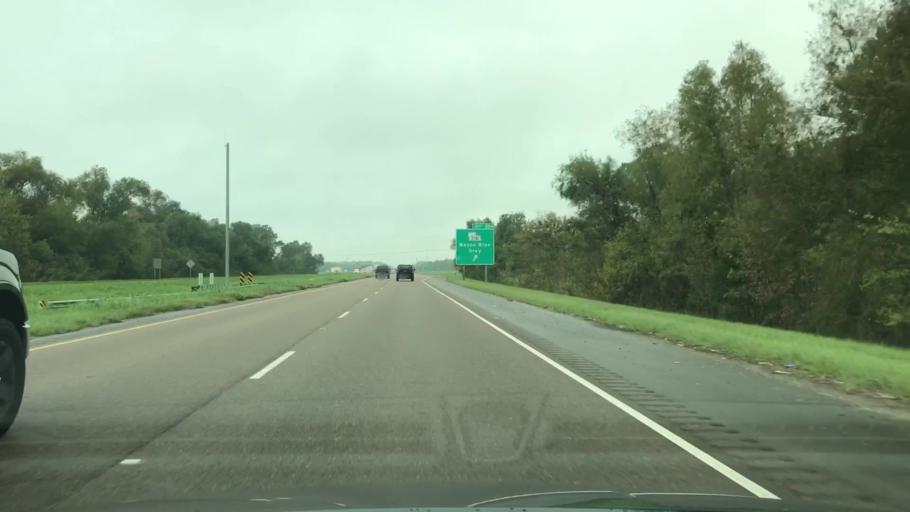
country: US
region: Louisiana
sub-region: Terrebonne Parish
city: Gray
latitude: 29.6837
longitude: -90.7414
